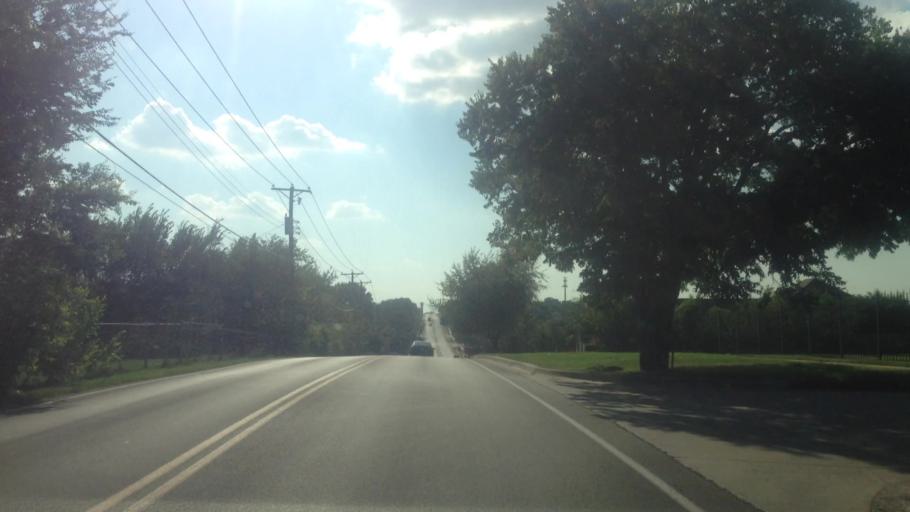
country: US
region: Texas
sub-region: Tarrant County
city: Watauga
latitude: 32.8678
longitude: -97.2525
